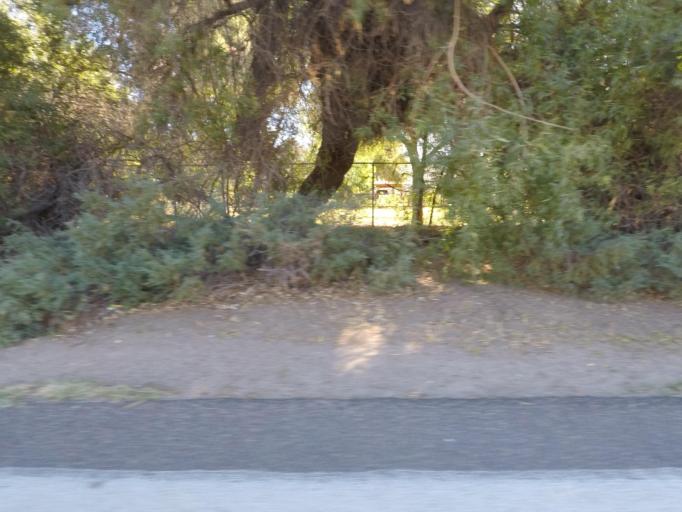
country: US
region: Arizona
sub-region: Maricopa County
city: Glendale
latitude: 33.5444
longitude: -112.1257
